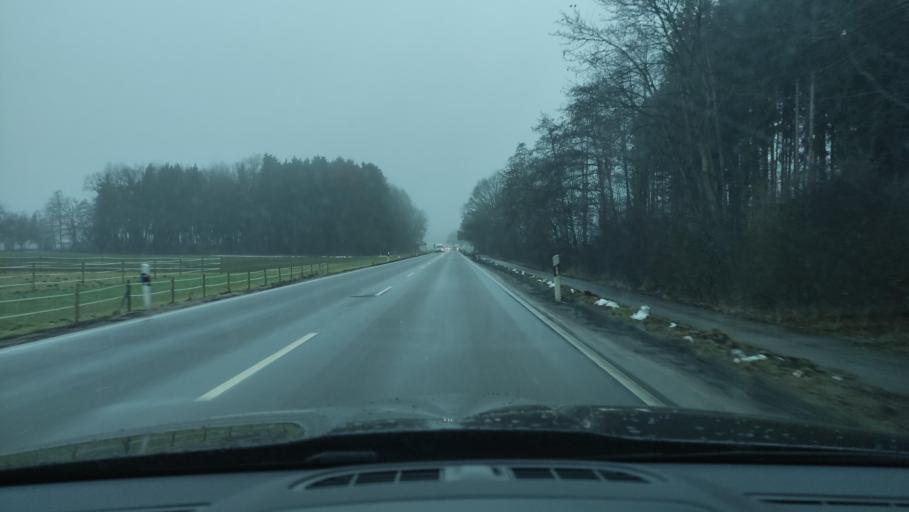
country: DE
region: Bavaria
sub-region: Swabia
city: Weissenhorn
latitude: 48.2930
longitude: 10.1369
